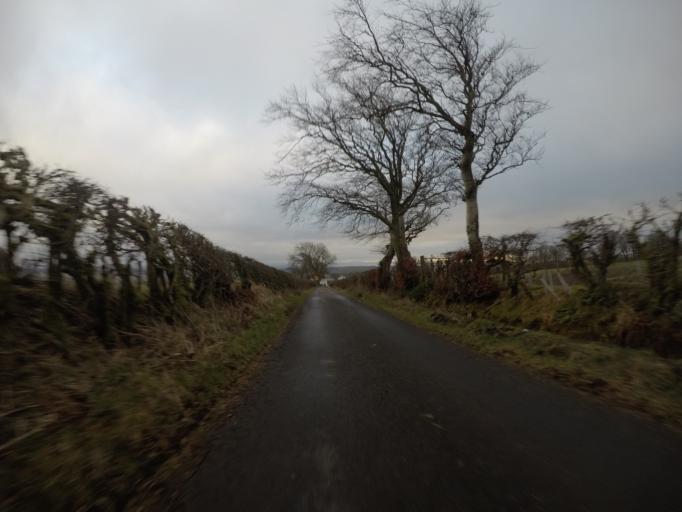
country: GB
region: Scotland
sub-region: North Ayrshire
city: Dalry
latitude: 55.7214
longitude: -4.7608
